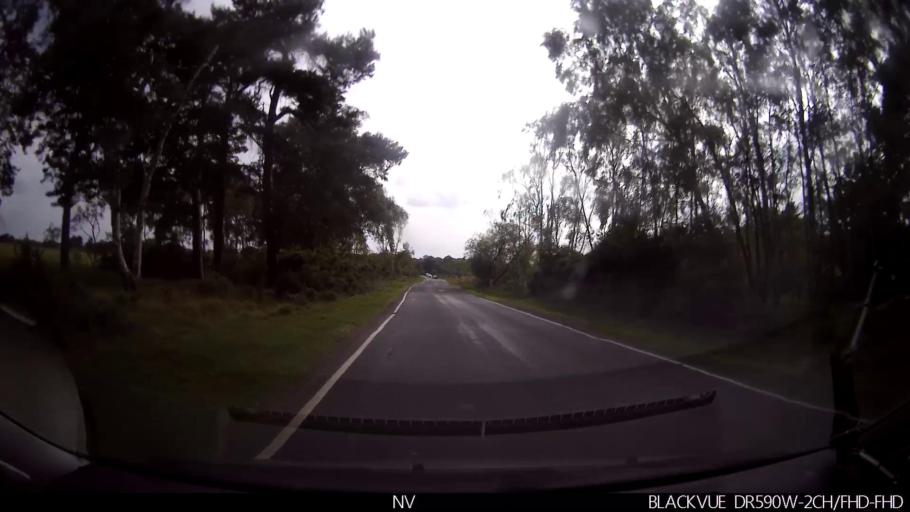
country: GB
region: England
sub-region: North Yorkshire
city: Strensall
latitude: 54.0476
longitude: -1.0053
